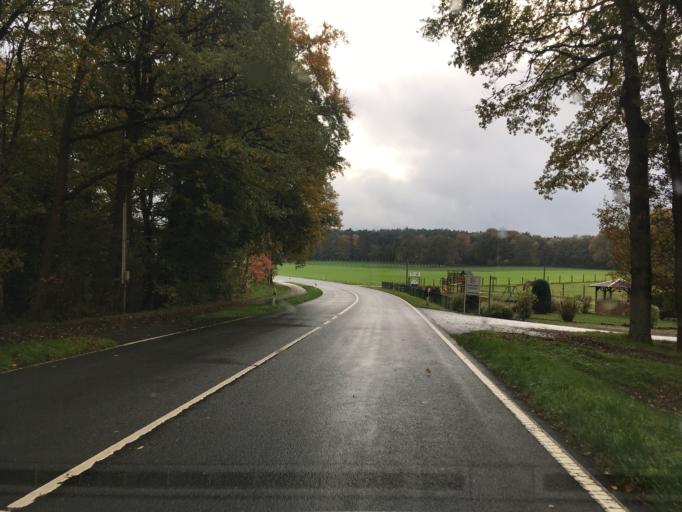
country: DE
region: North Rhine-Westphalia
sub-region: Regierungsbezirk Munster
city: Klein Reken
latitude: 51.8503
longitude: 7.0296
